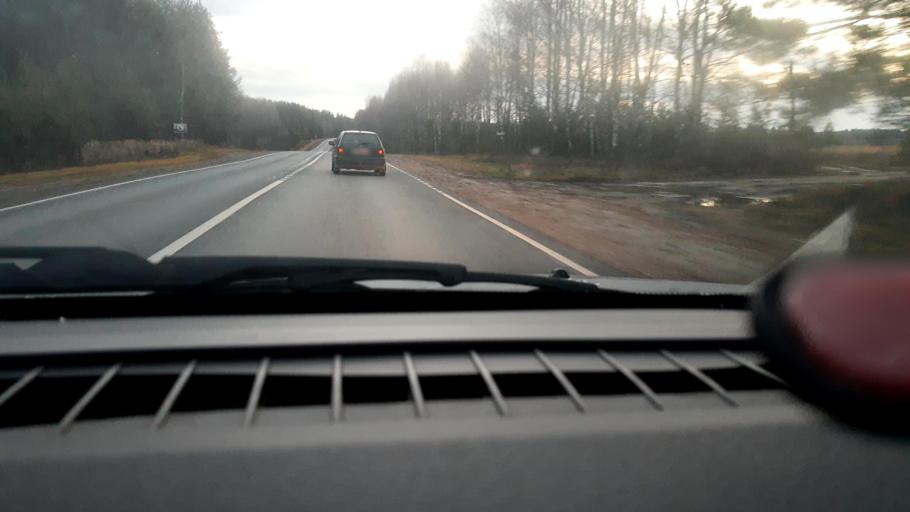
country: RU
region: Nizjnij Novgorod
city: Krasnyye Baki
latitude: 57.0370
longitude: 45.1246
